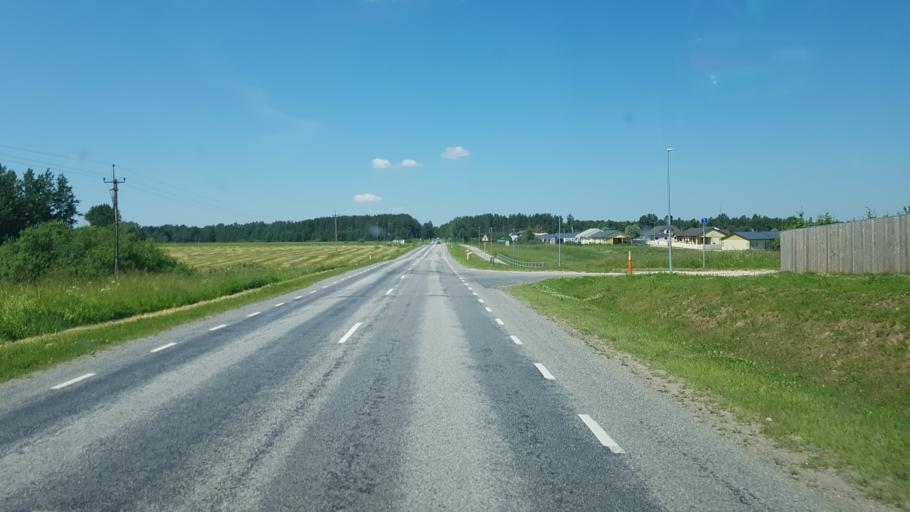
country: EE
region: Tartu
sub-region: UElenurme vald
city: Ulenurme
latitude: 58.3245
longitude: 26.7935
